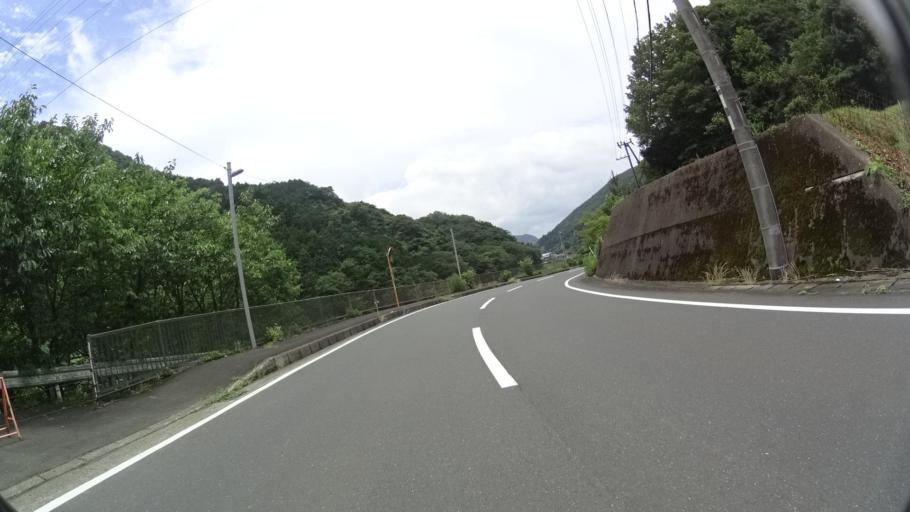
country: JP
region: Kyoto
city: Maizuru
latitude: 35.5202
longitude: 135.3606
